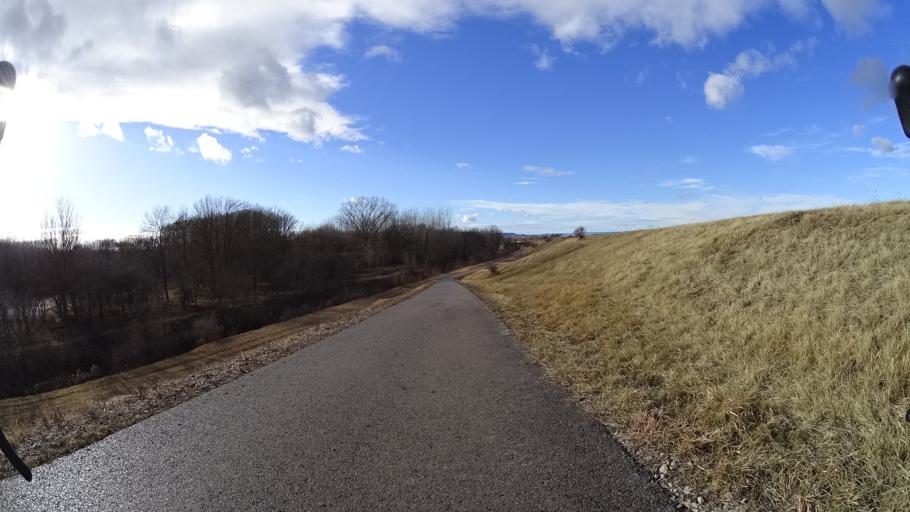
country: AT
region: Lower Austria
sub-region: Politischer Bezirk Tulln
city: Grafenworth
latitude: 48.3789
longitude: 15.8344
